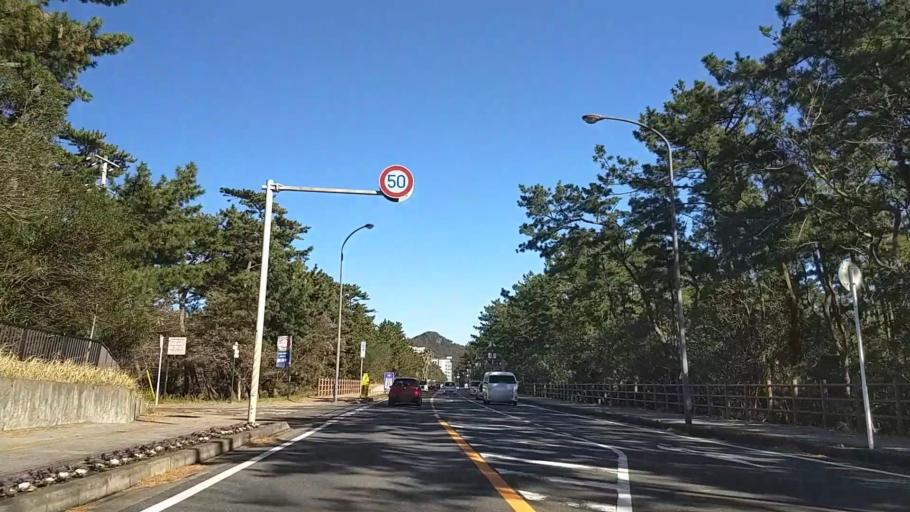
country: JP
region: Chiba
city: Kawaguchi
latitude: 35.1153
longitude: 140.1181
